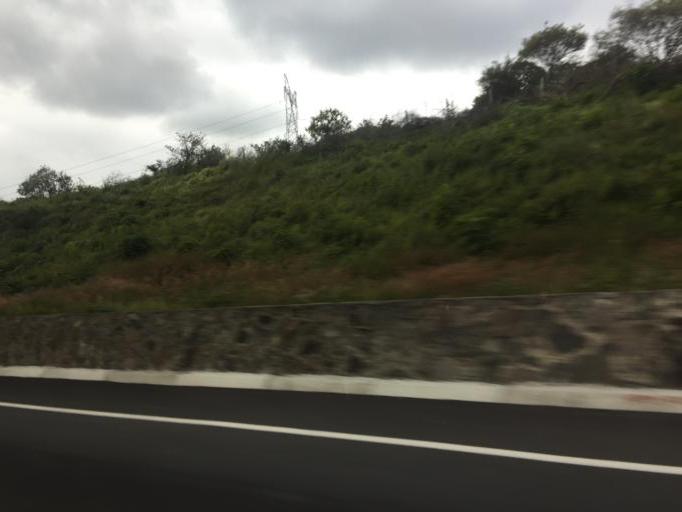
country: MX
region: Jalisco
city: Ocotlan
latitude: 20.4252
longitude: -102.7720
